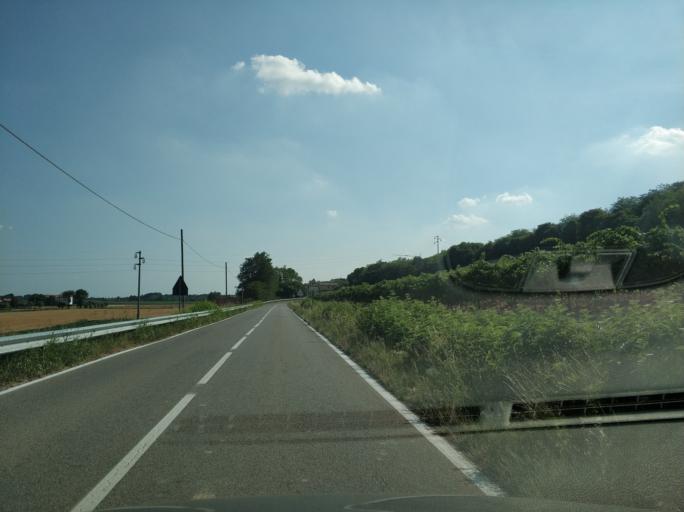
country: IT
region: Veneto
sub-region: Provincia di Padova
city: Baone
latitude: 45.2410
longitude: 11.7101
